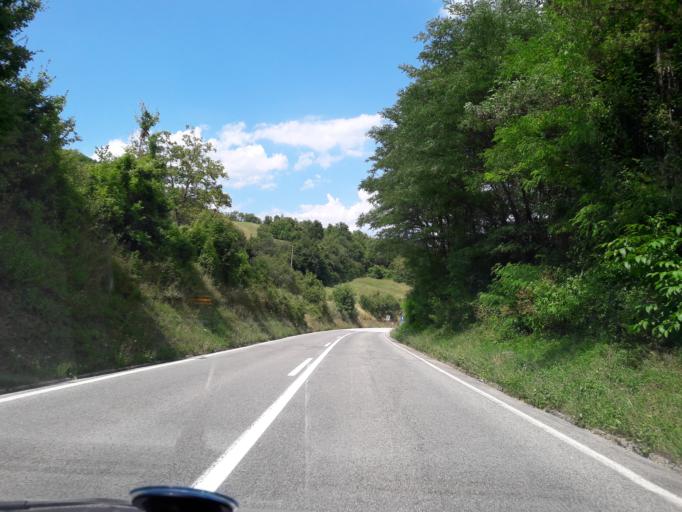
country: BA
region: Republika Srpska
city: Mrkonjic Grad
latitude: 44.5047
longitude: 17.1506
